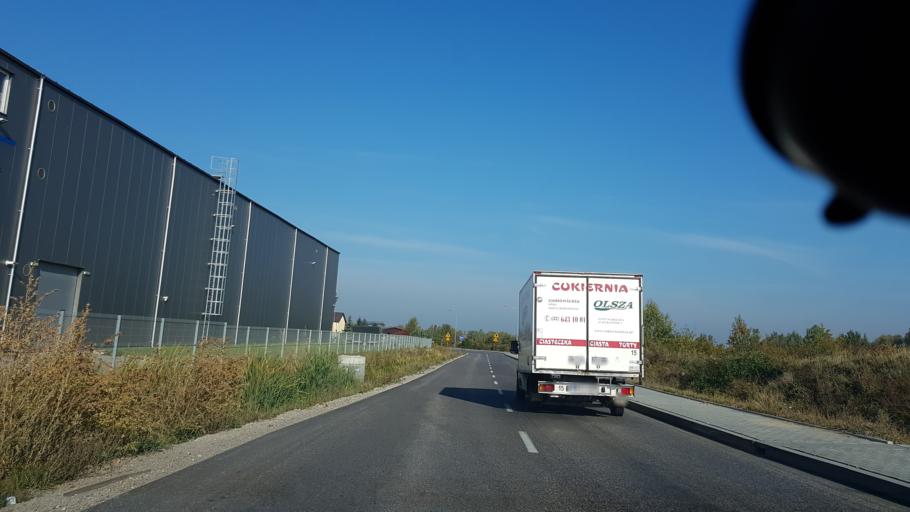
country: PL
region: Masovian Voivodeship
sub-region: Powiat pruszkowski
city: Nadarzyn
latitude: 52.0753
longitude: 20.7731
